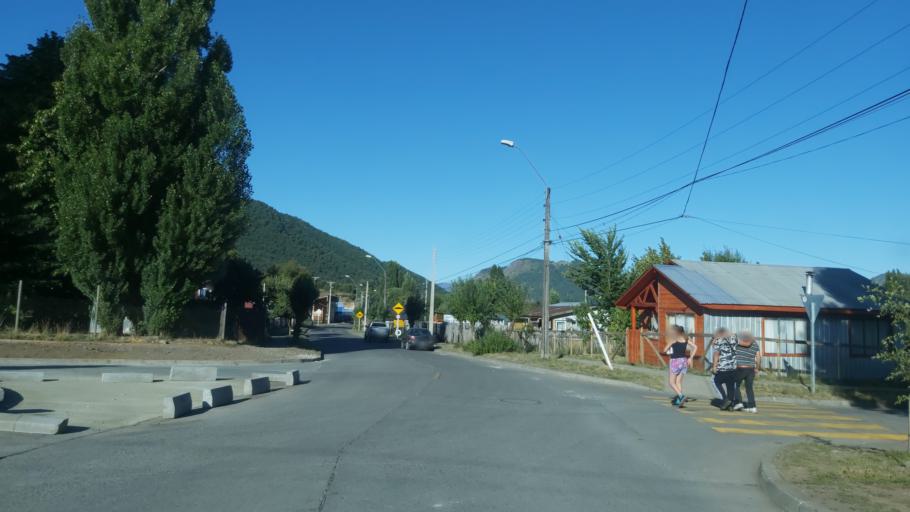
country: AR
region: Neuquen
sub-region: Departamento de Loncopue
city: Loncopue
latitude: -38.4501
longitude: -71.3709
